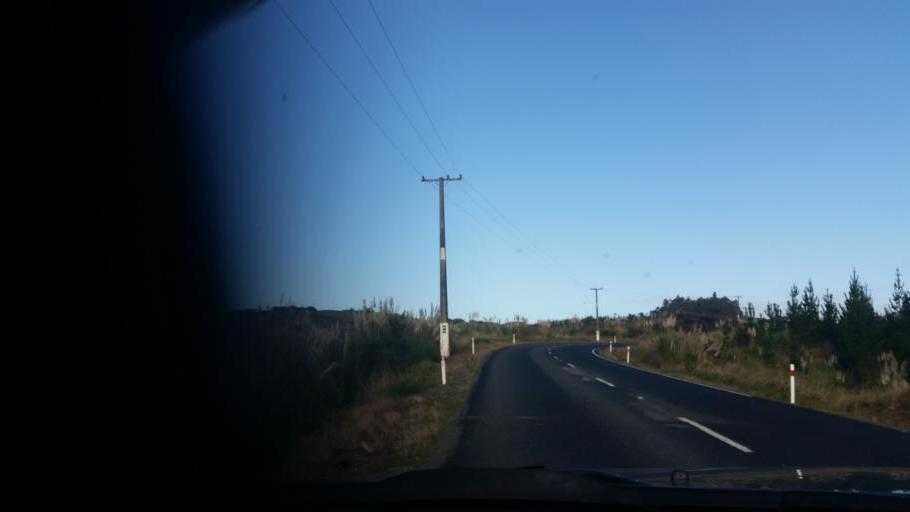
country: NZ
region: Auckland
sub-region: Auckland
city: Wellsford
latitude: -36.2194
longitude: 174.4638
